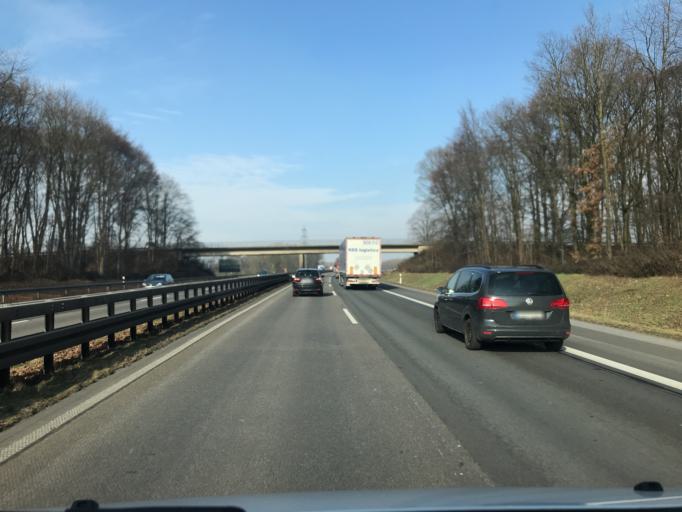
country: DE
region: North Rhine-Westphalia
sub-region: Regierungsbezirk Dusseldorf
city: Viersen
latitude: 51.2281
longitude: 6.3635
